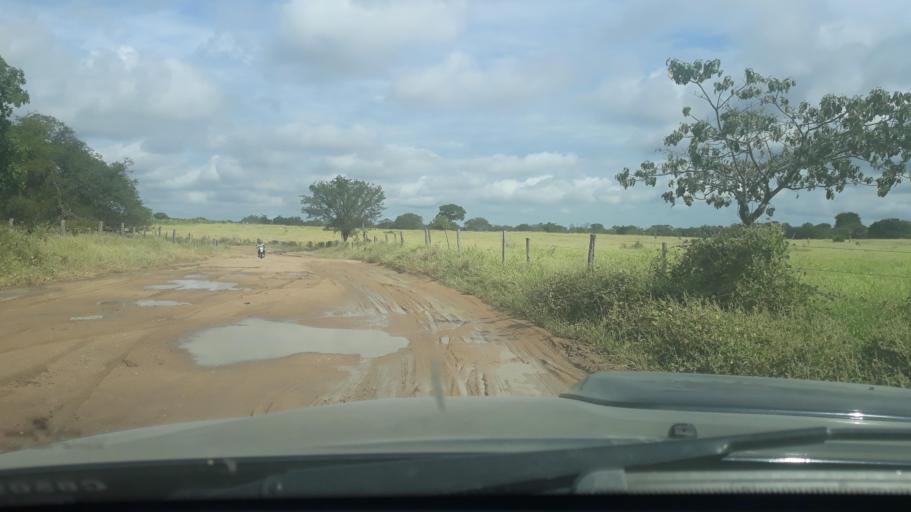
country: BR
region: Bahia
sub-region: Riacho De Santana
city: Riacho de Santana
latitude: -13.8992
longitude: -42.8759
